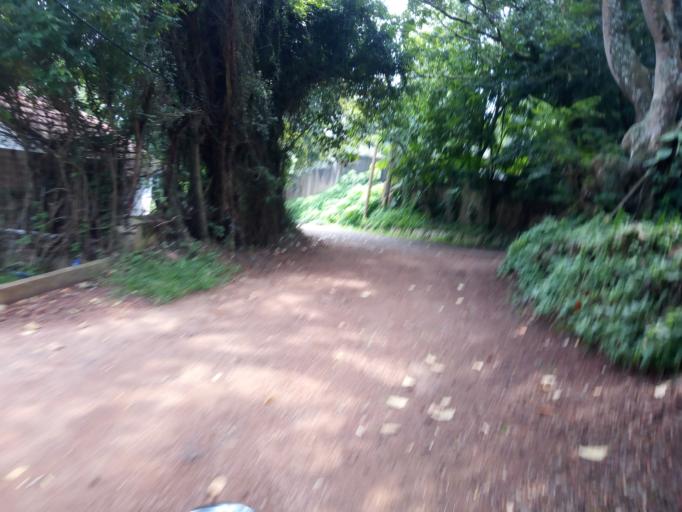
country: UG
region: Central Region
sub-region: Wakiso District
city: Kireka
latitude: 0.3232
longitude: 32.6267
